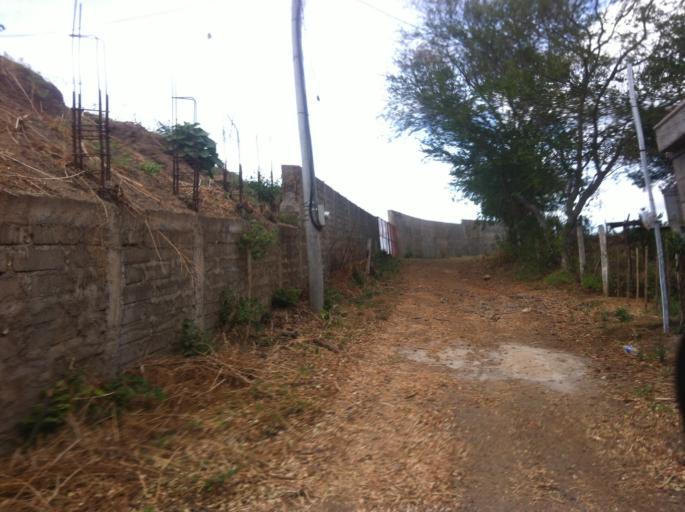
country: NI
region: Managua
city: Ciudad Sandino
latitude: 12.0850
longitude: -86.3256
